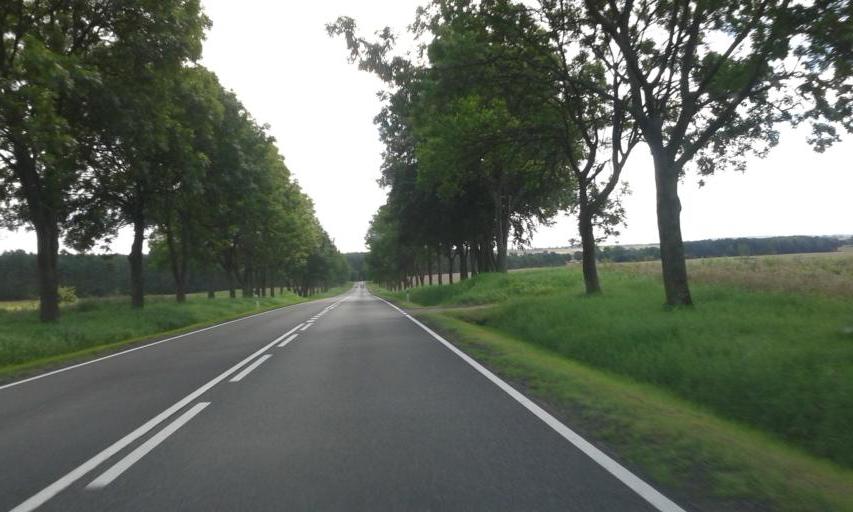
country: PL
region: West Pomeranian Voivodeship
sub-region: Powiat walecki
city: Walcz
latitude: 53.2513
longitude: 16.5252
